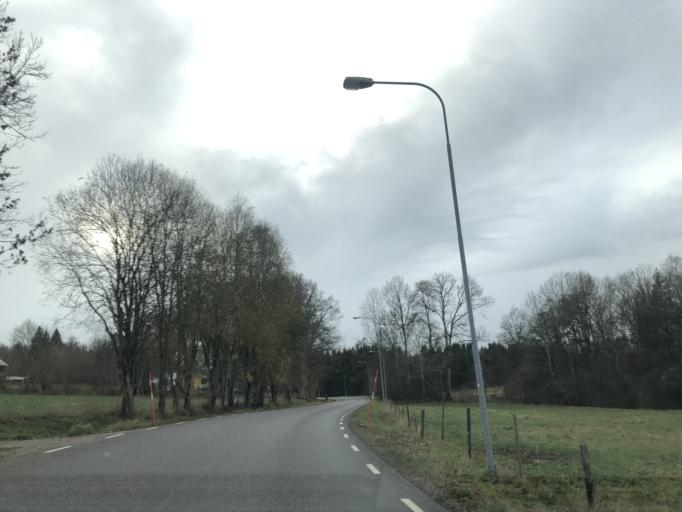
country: SE
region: Vaestra Goetaland
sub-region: Ulricehamns Kommun
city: Ulricehamn
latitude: 57.6807
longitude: 13.4121
